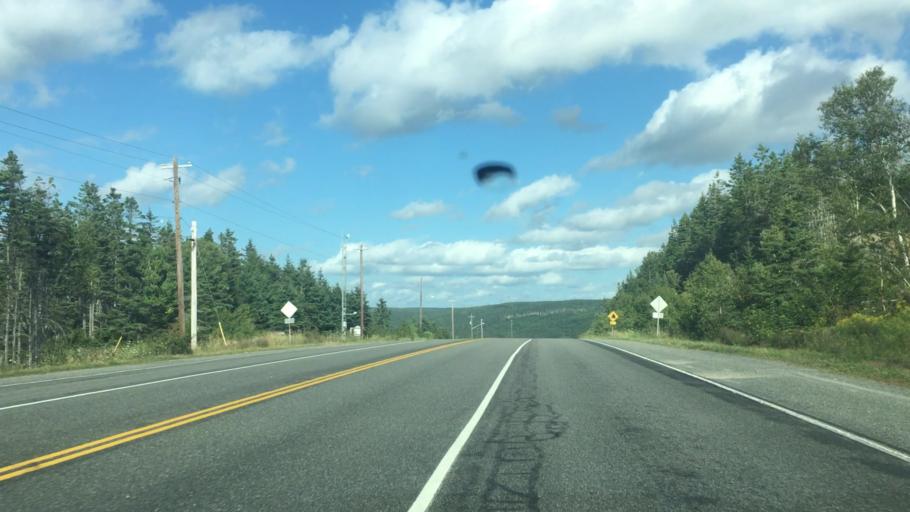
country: CA
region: Nova Scotia
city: Sydney
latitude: 45.8146
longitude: -60.6941
